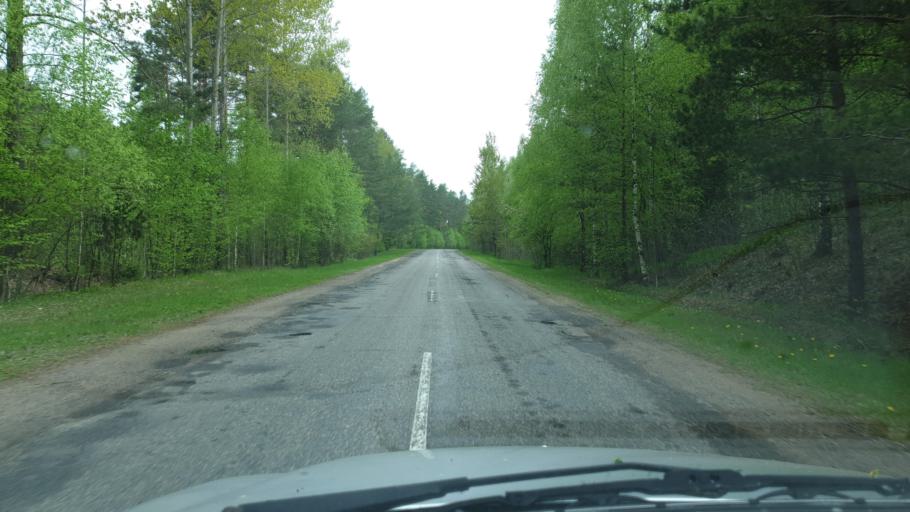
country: BY
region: Vitebsk
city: Lyepyel'
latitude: 54.9005
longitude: 28.5790
